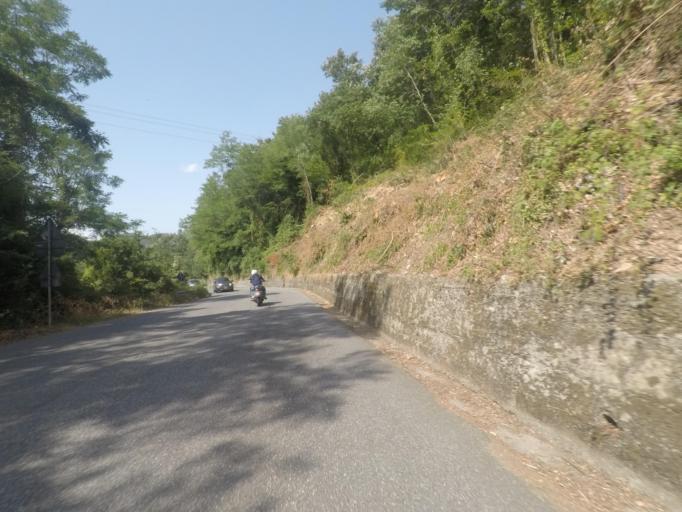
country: IT
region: Tuscany
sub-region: Provincia di Massa-Carrara
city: Fivizzano
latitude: 44.1724
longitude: 10.1153
